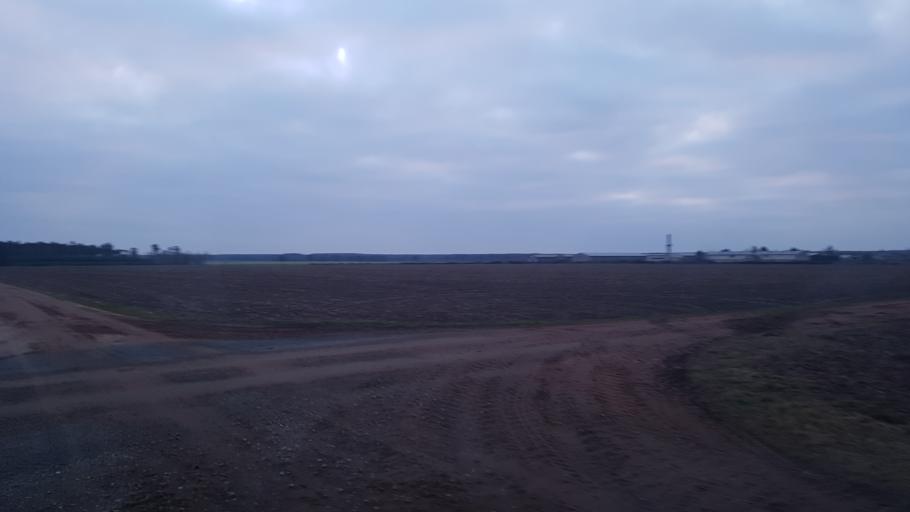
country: DE
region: Saxony-Anhalt
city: Holzdorf
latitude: 51.8581
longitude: 13.1228
